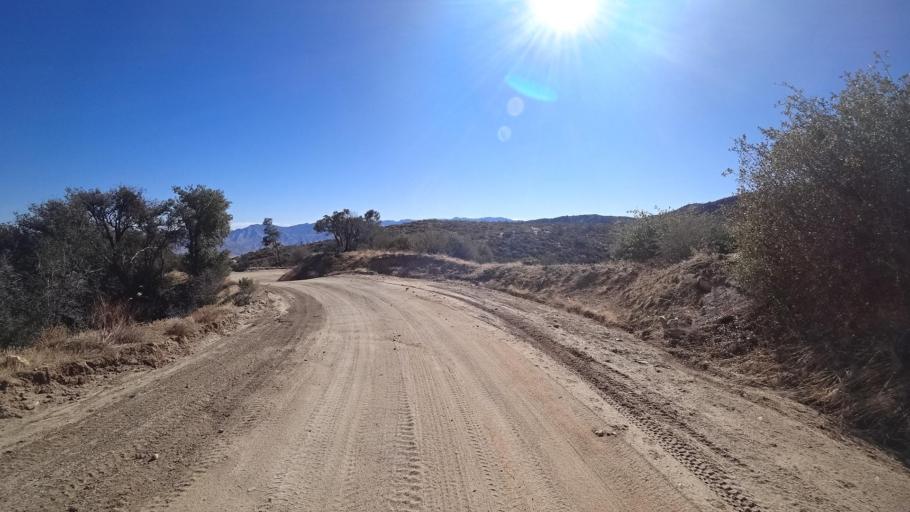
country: US
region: California
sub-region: Kern County
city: Alta Sierra
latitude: 35.7128
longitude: -118.5153
